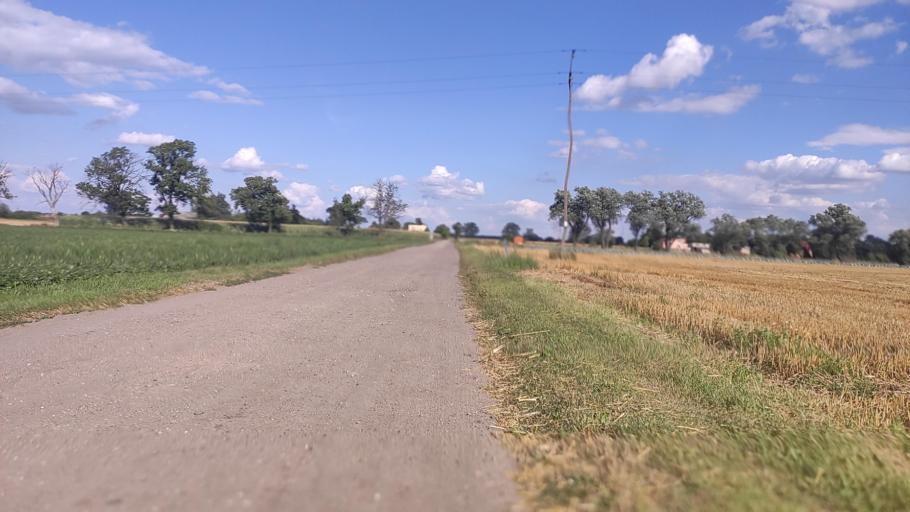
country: PL
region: Greater Poland Voivodeship
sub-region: Powiat poznanski
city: Swarzedz
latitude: 52.4110
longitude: 17.1343
